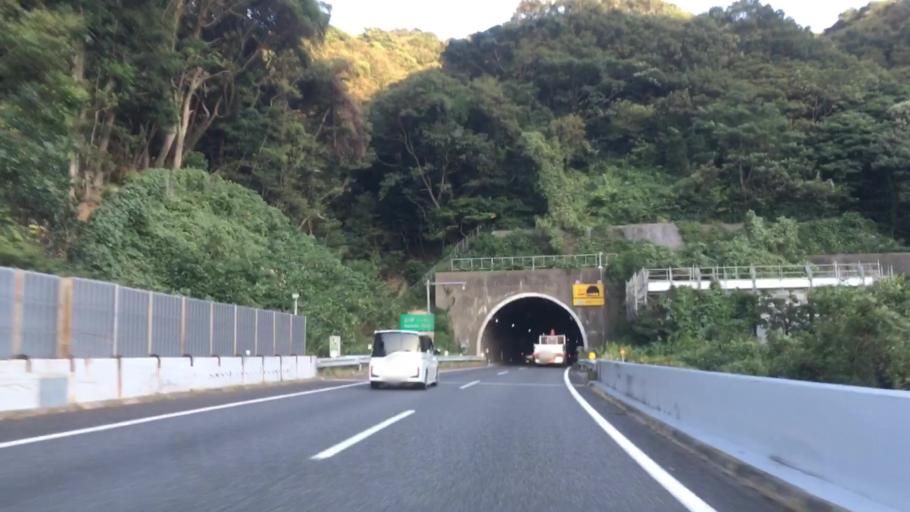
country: JP
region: Yamaguchi
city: Shimonoseki
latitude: 33.9508
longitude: 130.9902
